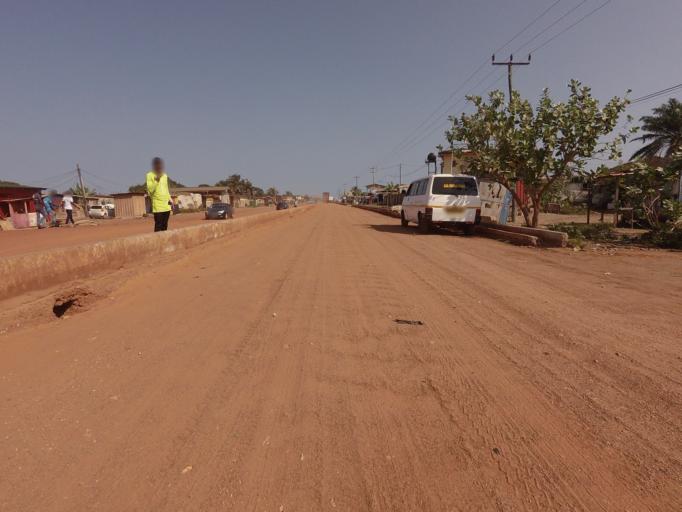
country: GH
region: Greater Accra
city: Teshi Old Town
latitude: 5.5847
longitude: -0.1140
